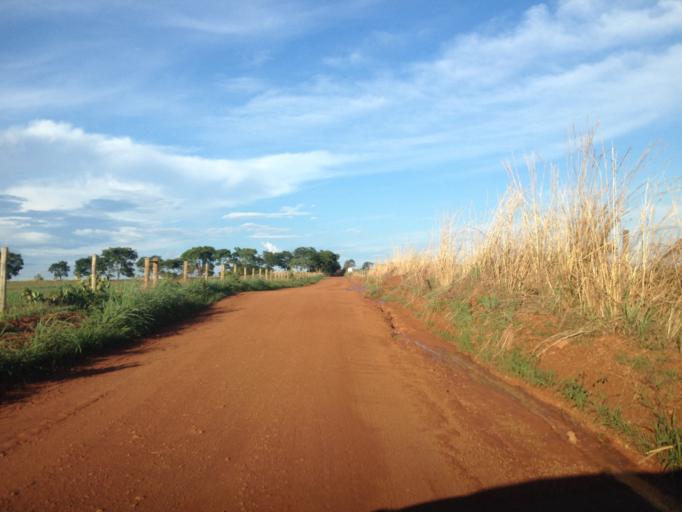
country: BR
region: Goias
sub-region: Abadiania
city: Abadiania
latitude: -15.9932
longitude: -48.5380
